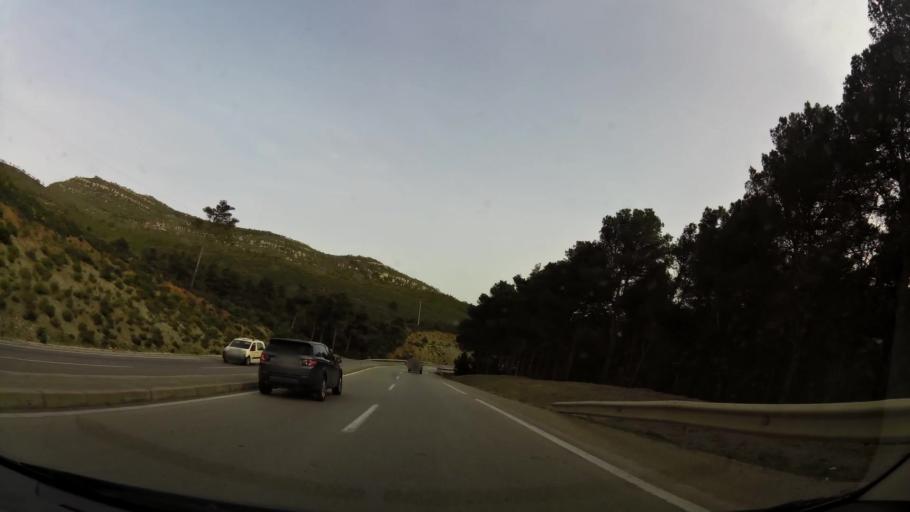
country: MA
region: Tanger-Tetouan
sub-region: Tetouan
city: Saddina
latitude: 35.5584
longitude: -5.5692
